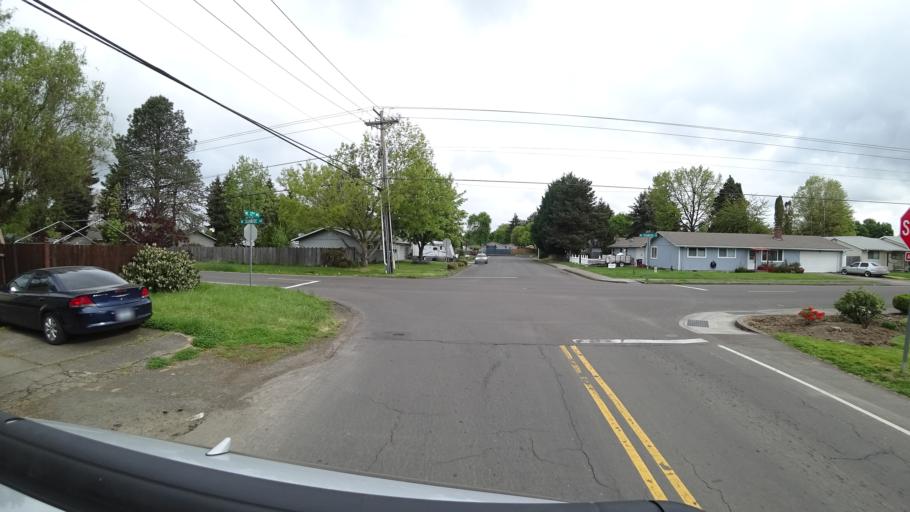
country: US
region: Oregon
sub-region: Washington County
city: Hillsboro
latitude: 45.5365
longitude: -122.9646
